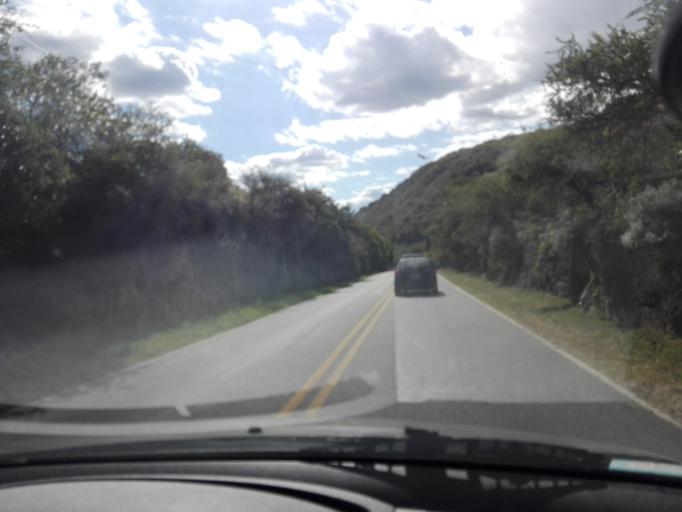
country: AR
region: Cordoba
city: Villa Las Rosas
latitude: -31.9089
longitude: -64.9970
